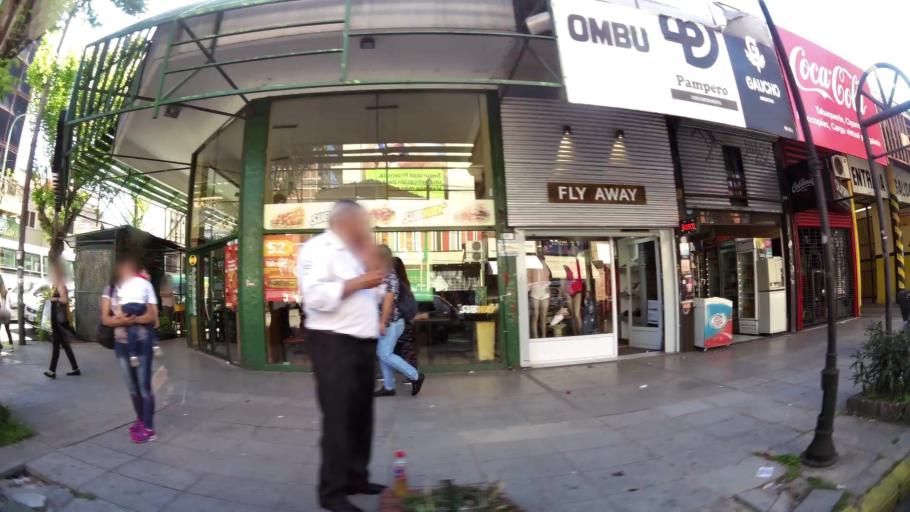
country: AR
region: Buenos Aires
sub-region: Partido de Lomas de Zamora
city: Lomas de Zamora
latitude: -34.7616
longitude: -58.4012
